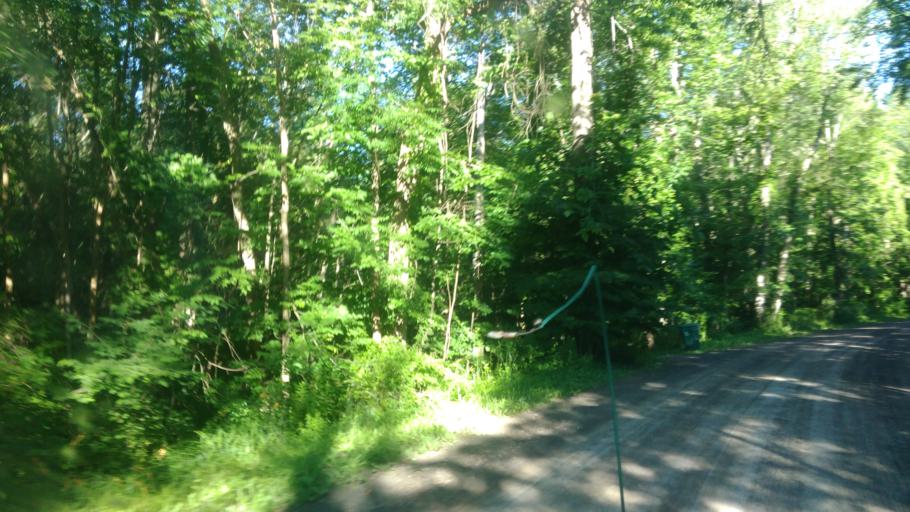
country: US
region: New York
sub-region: Wayne County
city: Sodus
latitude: 43.1626
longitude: -77.0566
